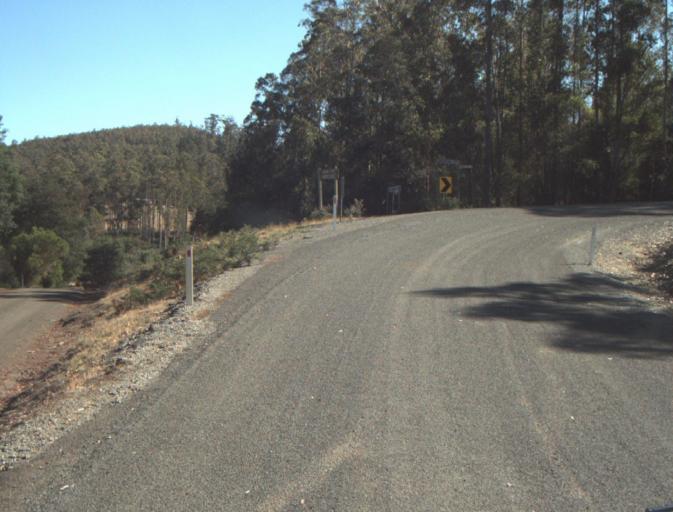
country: AU
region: Tasmania
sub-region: Dorset
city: Scottsdale
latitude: -41.2911
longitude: 147.3407
